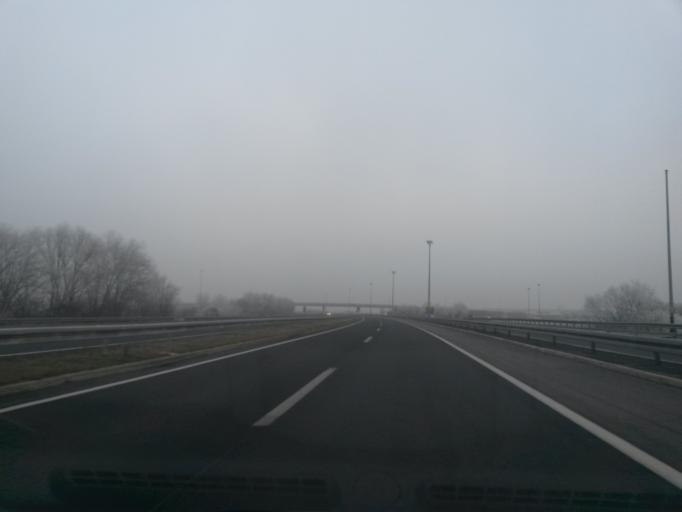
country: HR
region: Zagrebacka
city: Brckovljani
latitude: 45.9011
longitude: 16.2687
